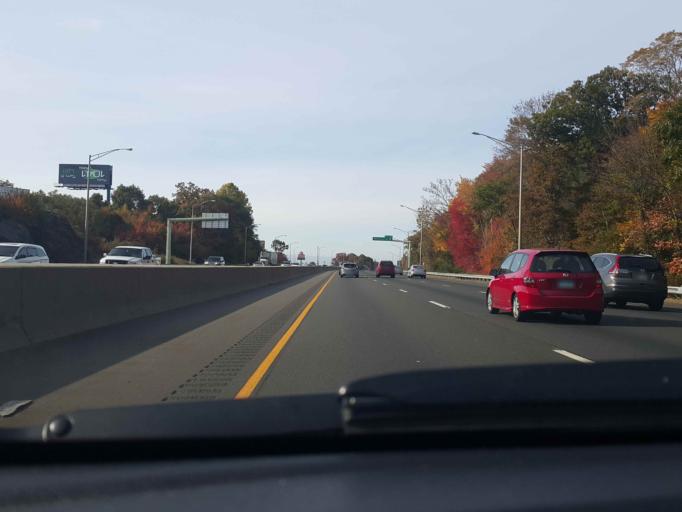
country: US
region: Connecticut
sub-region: New Haven County
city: Woodmont
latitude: 41.2422
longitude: -73.0160
